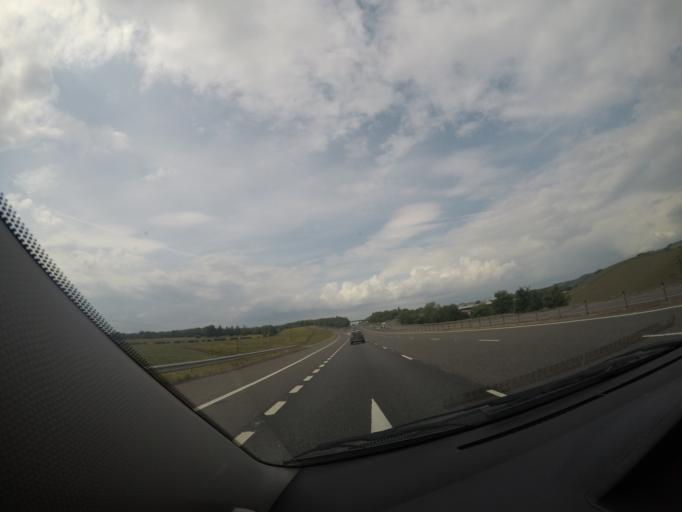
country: GB
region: Scotland
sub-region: Dumfries and Galloway
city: Lockerbie
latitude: 55.1287
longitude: -3.3669
